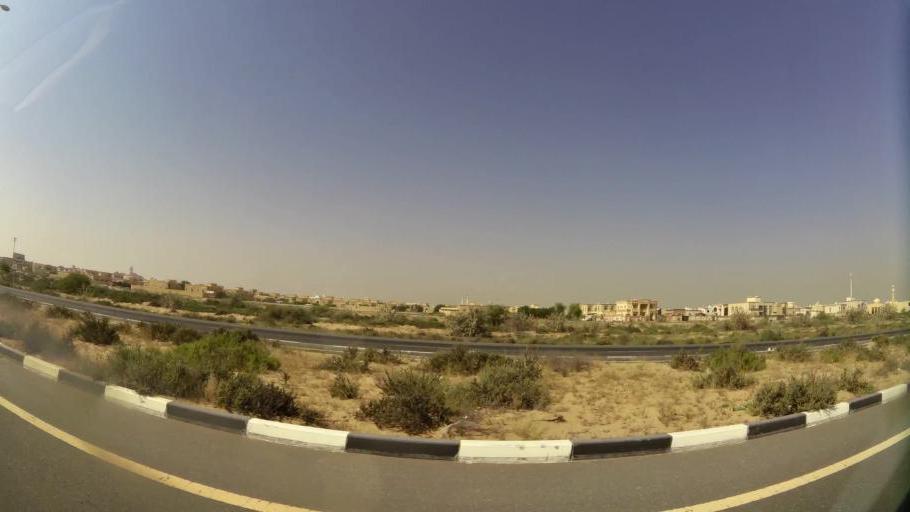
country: AE
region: Ajman
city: Ajman
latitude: 25.4187
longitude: 55.5417
